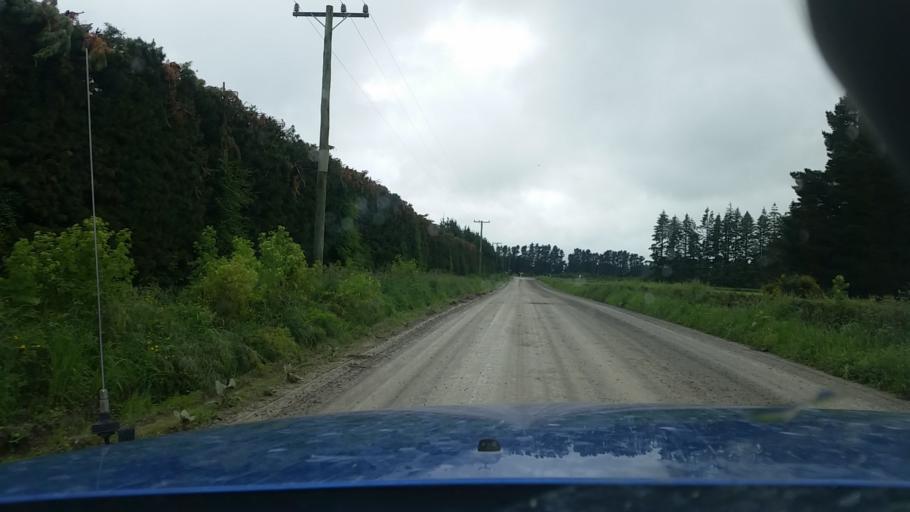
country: NZ
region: Canterbury
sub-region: Ashburton District
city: Methven
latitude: -43.6137
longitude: 171.4886
